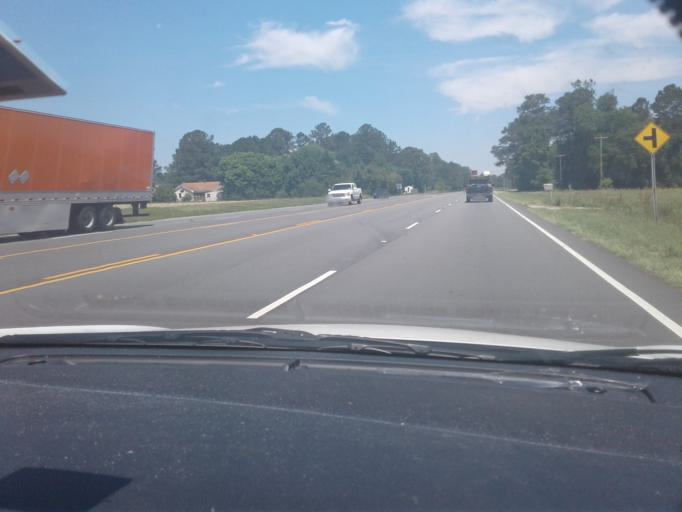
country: US
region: North Carolina
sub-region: Harnett County
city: Buies Creek
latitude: 35.3911
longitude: -78.7278
